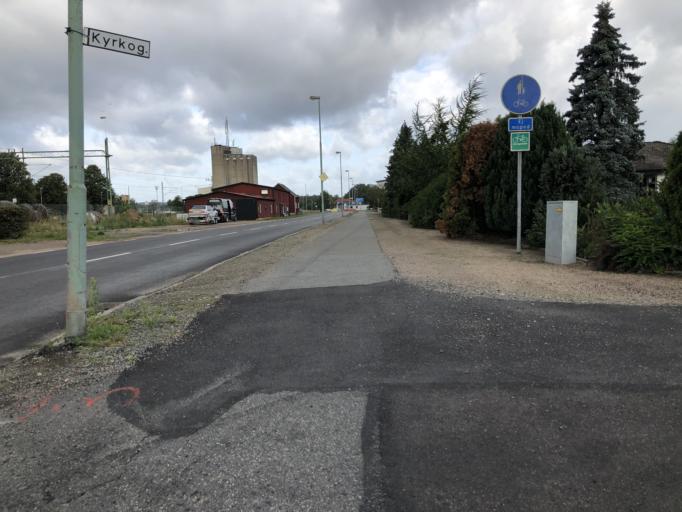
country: SE
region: Skane
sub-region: Hassleholms Kommun
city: Vinslov
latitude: 56.1053
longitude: 13.9165
